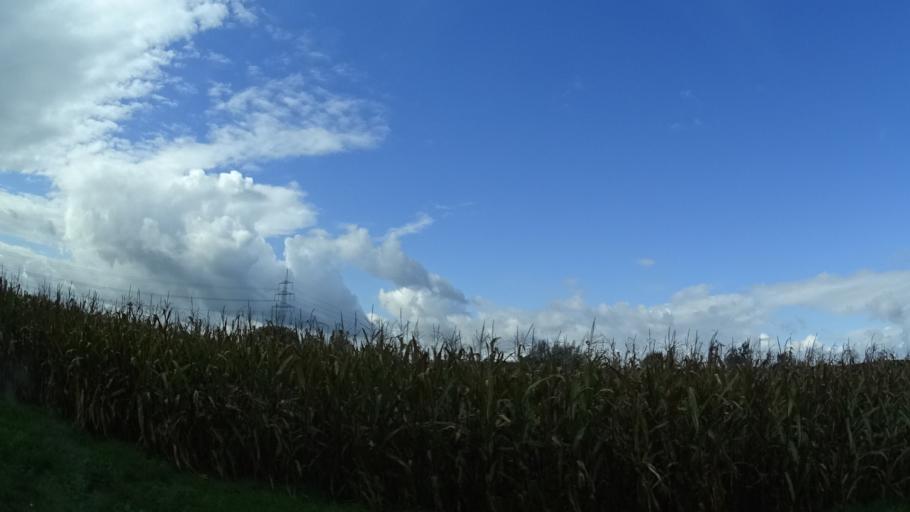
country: DE
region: Bavaria
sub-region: Regierungsbezirk Unterfranken
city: Lulsfeld
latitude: 49.8661
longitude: 10.3142
